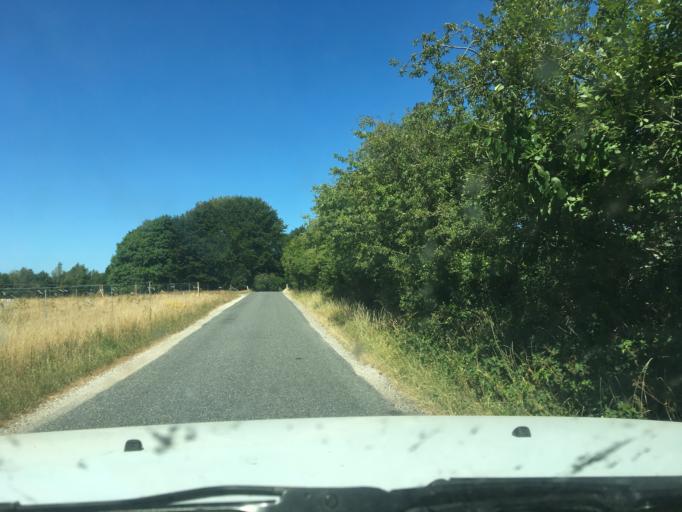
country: DK
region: Central Jutland
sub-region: Syddjurs Kommune
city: Ryomgard
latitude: 56.4811
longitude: 10.5939
